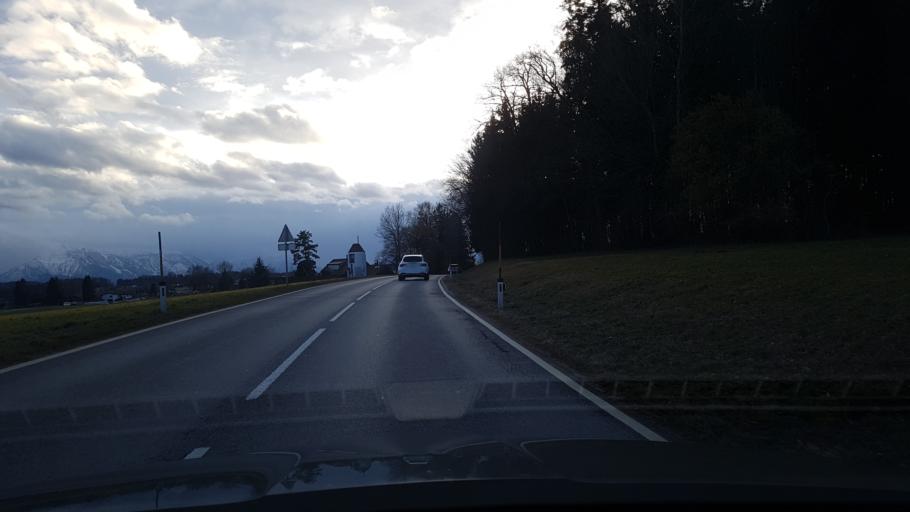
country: AT
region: Salzburg
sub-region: Politischer Bezirk Salzburg-Umgebung
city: Seekirchen am Wallersee
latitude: 47.9061
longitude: 13.1294
